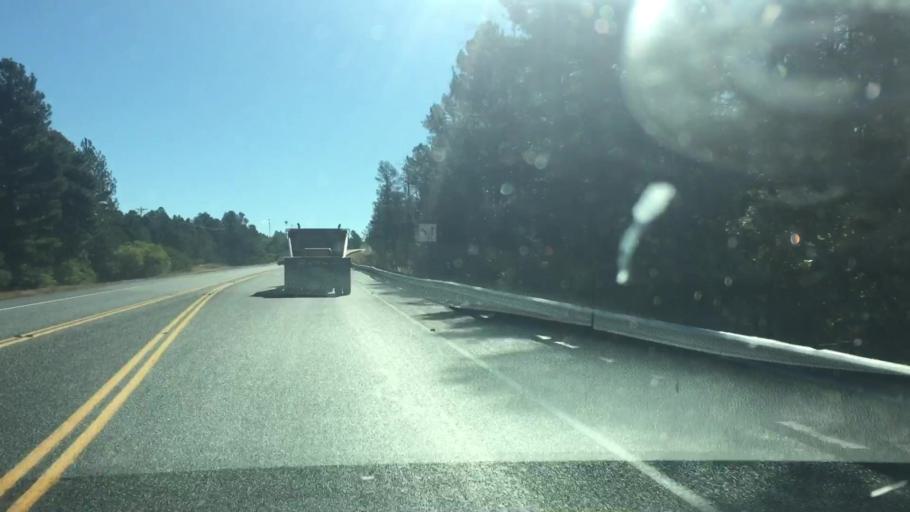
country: US
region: Colorado
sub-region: Elbert County
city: Ponderosa Park
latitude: 39.3769
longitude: -104.6954
